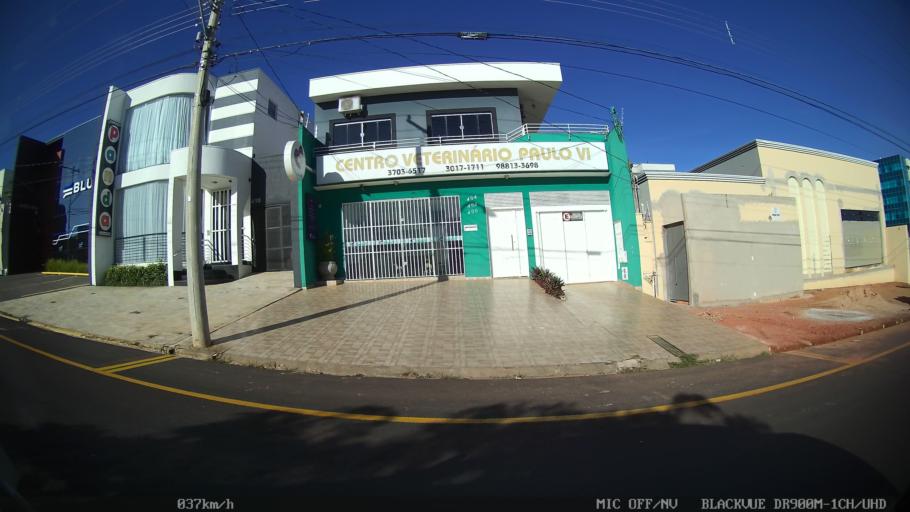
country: BR
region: Sao Paulo
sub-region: Franca
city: Franca
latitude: -20.5562
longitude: -47.4071
